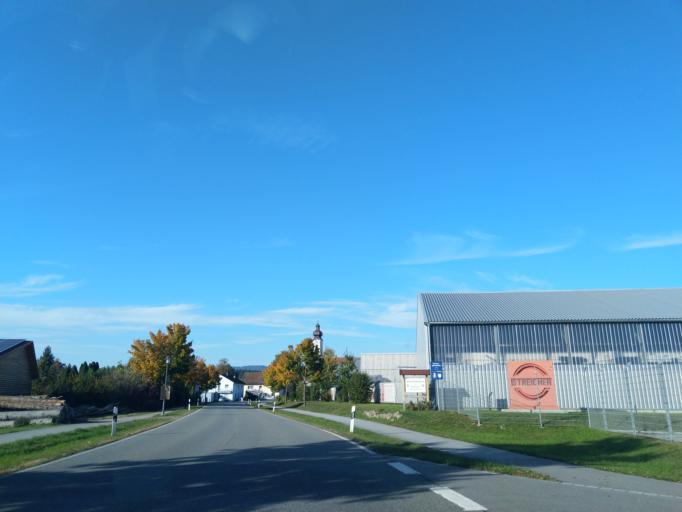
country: DE
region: Bavaria
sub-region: Lower Bavaria
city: Metten
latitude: 48.8589
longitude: 12.8929
